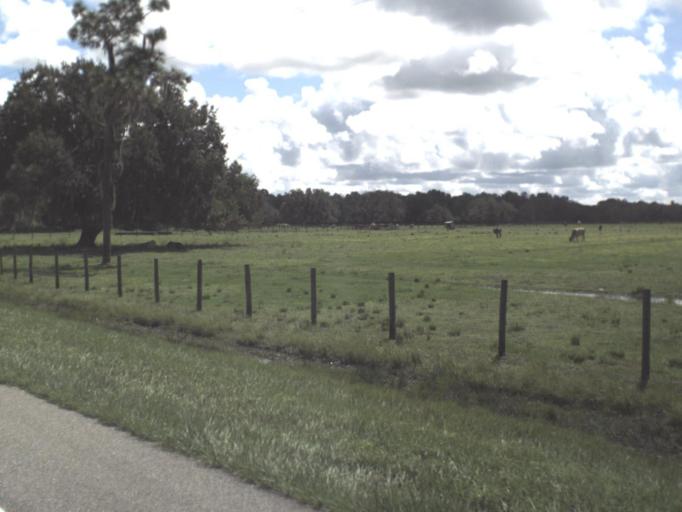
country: US
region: Florida
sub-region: Sarasota County
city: Lake Sarasota
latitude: 27.3616
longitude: -82.1977
